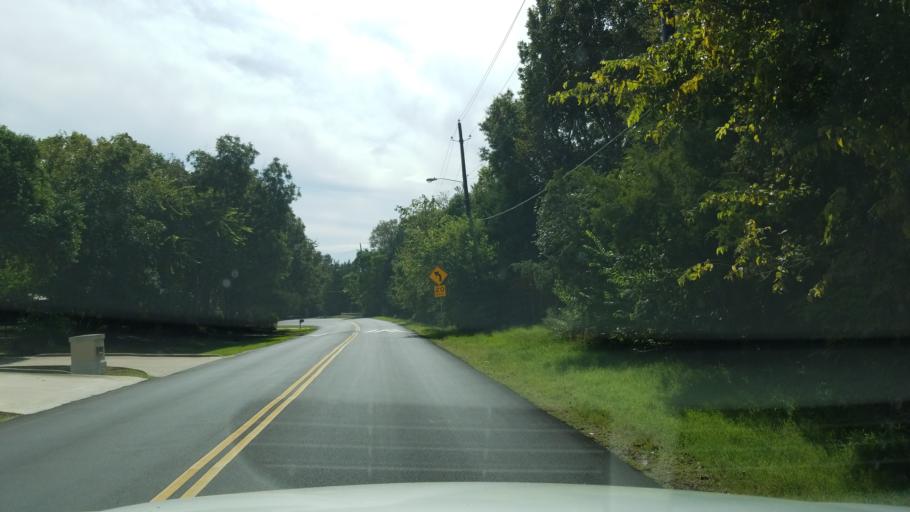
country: US
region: Texas
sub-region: Dallas County
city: Highland Park
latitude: 32.8111
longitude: -96.7231
